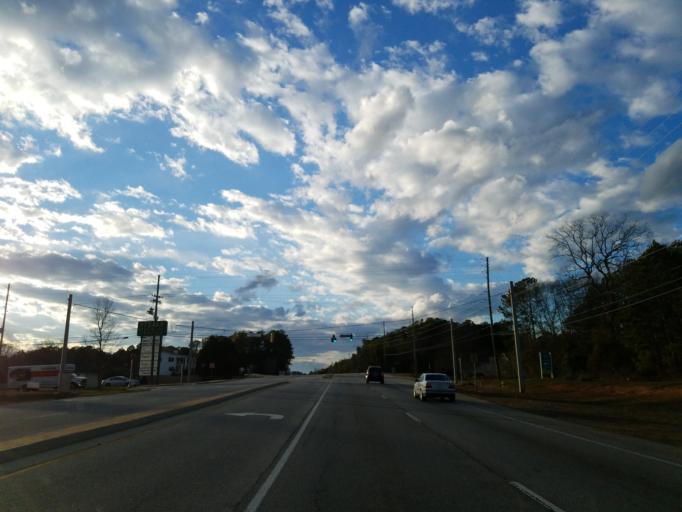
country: US
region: Georgia
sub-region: Henry County
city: McDonough
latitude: 33.4585
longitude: -84.1770
